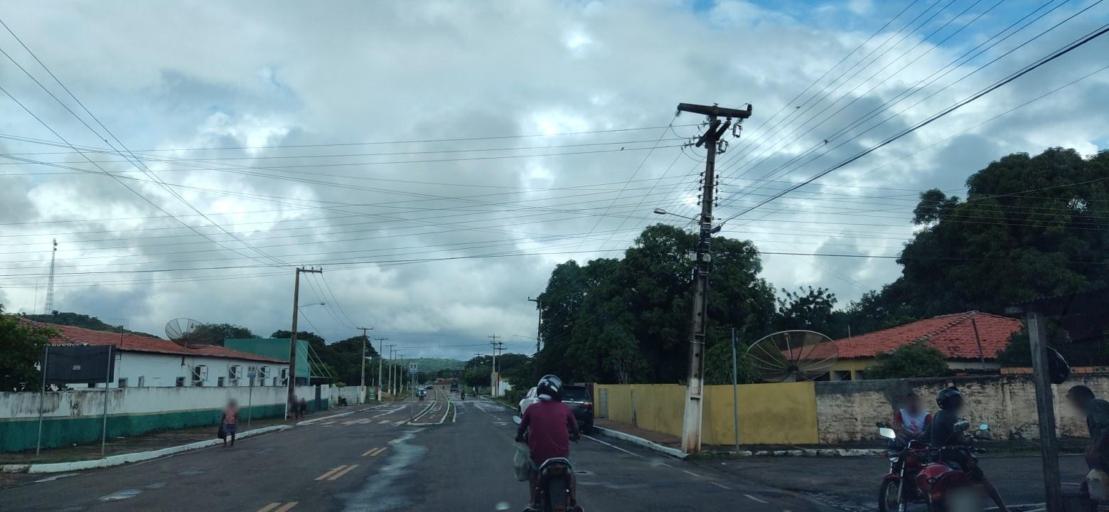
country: BR
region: Piaui
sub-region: Valenca Do Piaui
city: Valenca do Piaui
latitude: -6.1111
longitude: -41.7916
